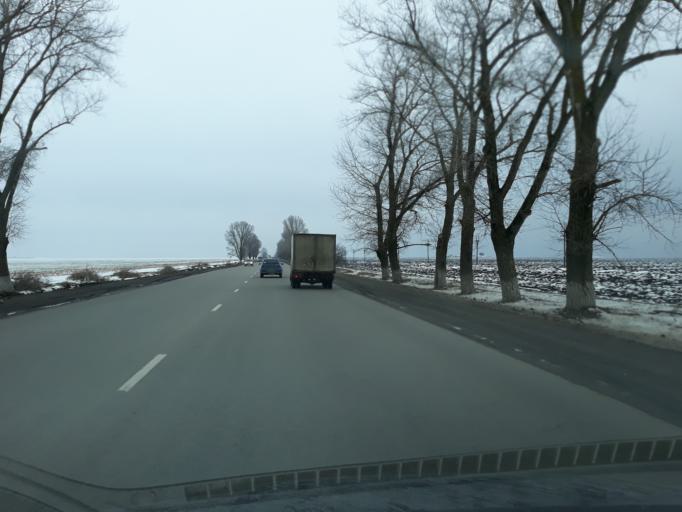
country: RU
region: Rostov
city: Primorka
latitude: 47.3048
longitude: 39.1569
